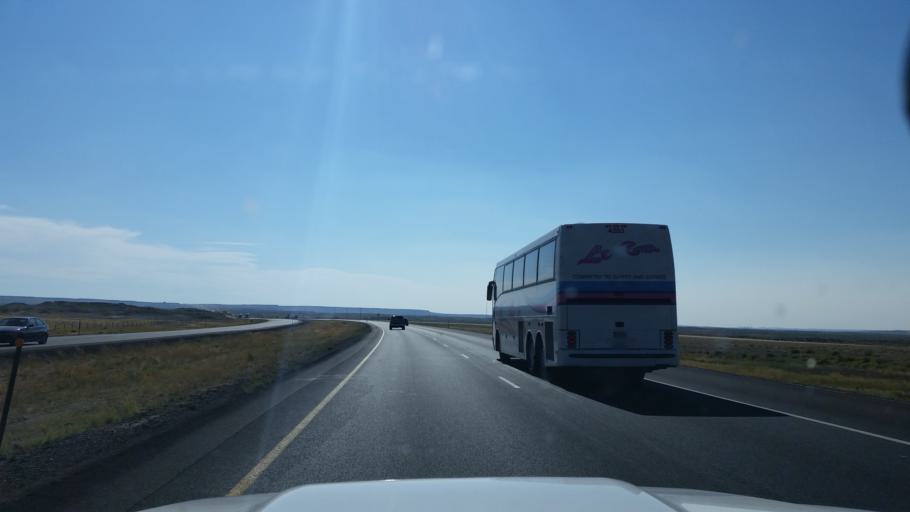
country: US
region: Wyoming
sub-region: Uinta County
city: Lyman
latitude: 41.5435
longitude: -109.9156
